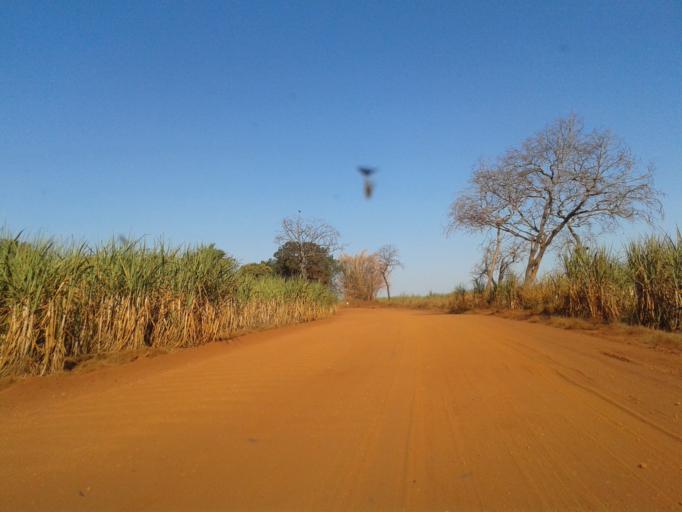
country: BR
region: Minas Gerais
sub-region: Santa Vitoria
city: Santa Vitoria
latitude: -18.8732
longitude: -50.0484
